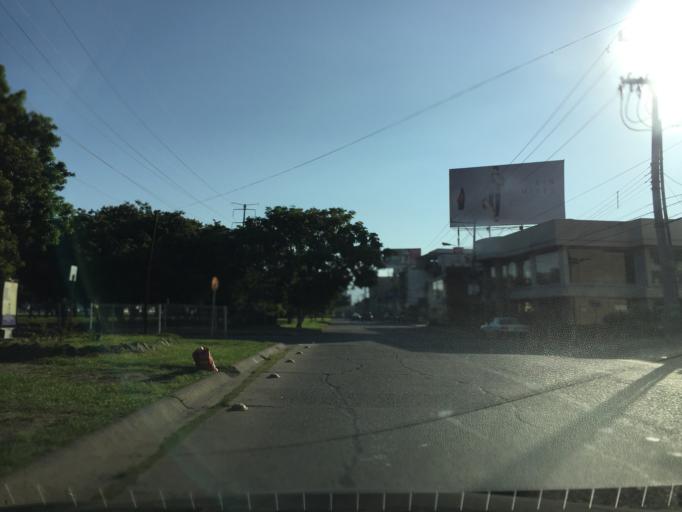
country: MX
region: Guanajuato
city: Leon
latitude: 21.1545
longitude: -101.6962
